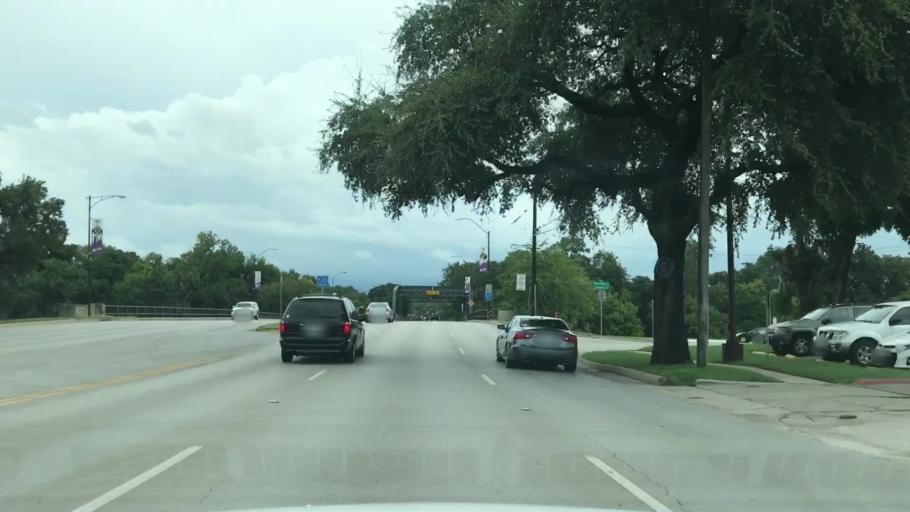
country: US
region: Texas
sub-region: Tarrant County
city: Fort Worth
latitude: 32.7257
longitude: -97.3613
